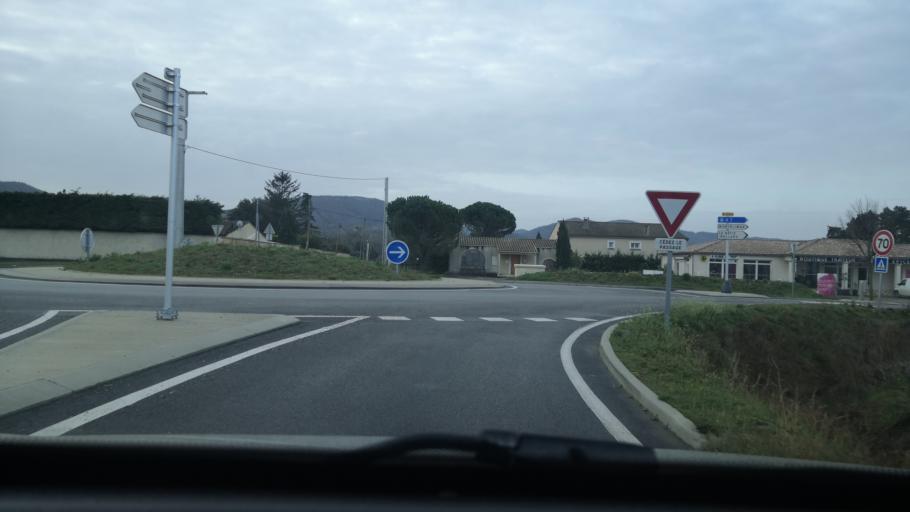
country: FR
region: Rhone-Alpes
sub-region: Departement de la Drome
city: La Begude-de-Mazenc
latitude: 44.5466
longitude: 4.9252
